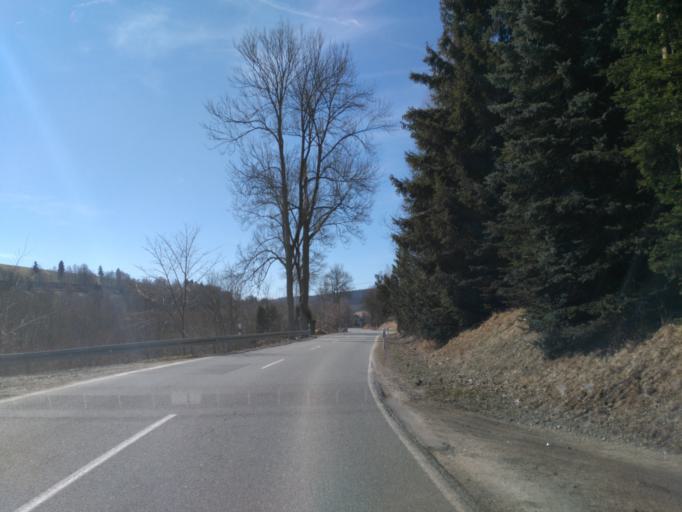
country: CZ
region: Ustecky
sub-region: Okres Chomutov
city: Vejprty
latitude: 50.4830
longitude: 13.0222
